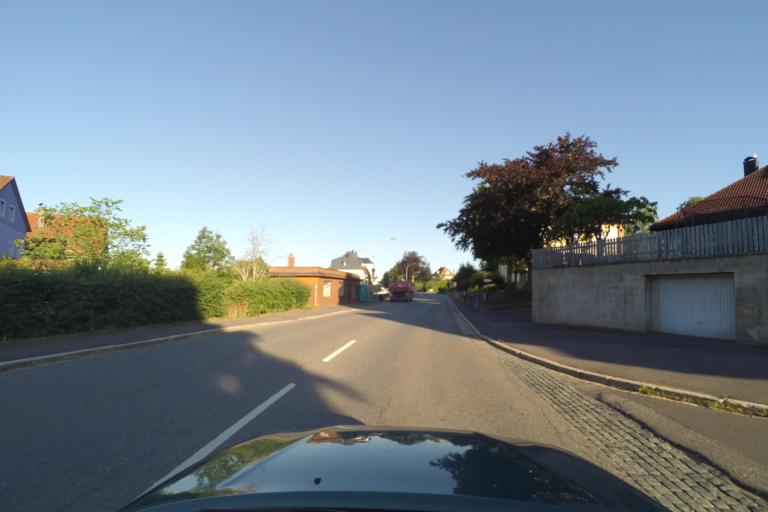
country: DE
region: Bavaria
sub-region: Upper Palatinate
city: Mitterteich
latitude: 49.9490
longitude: 12.2379
